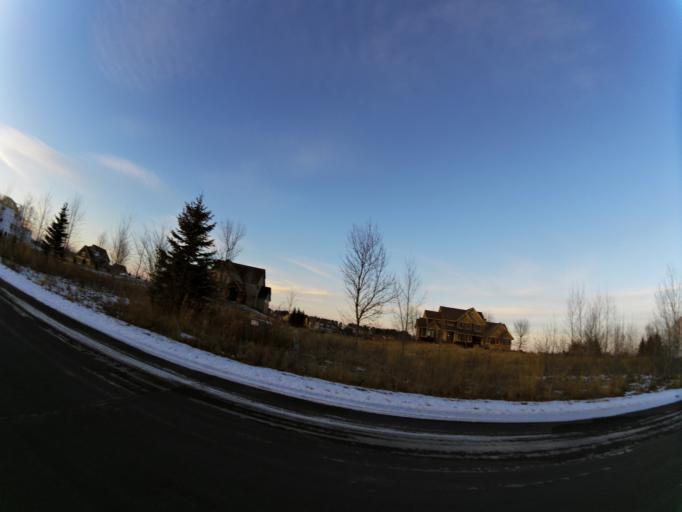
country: US
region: Minnesota
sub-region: Washington County
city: Lake Elmo
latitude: 44.9776
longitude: -92.8487
